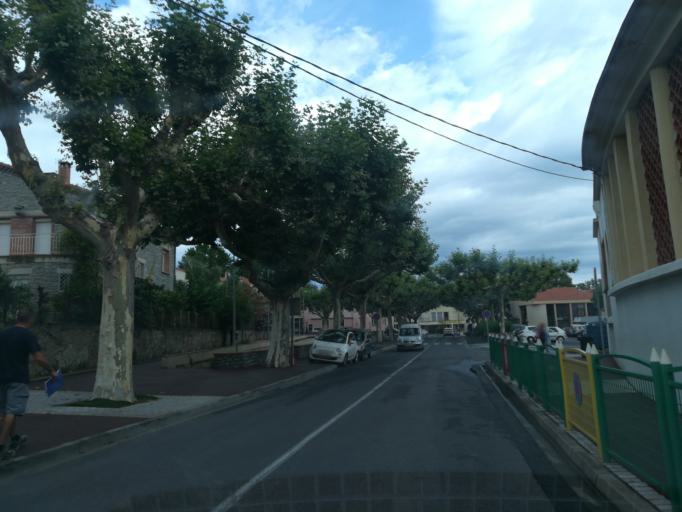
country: FR
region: Languedoc-Roussillon
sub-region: Departement des Pyrenees-Orientales
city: Ceret
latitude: 42.4862
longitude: 2.7513
